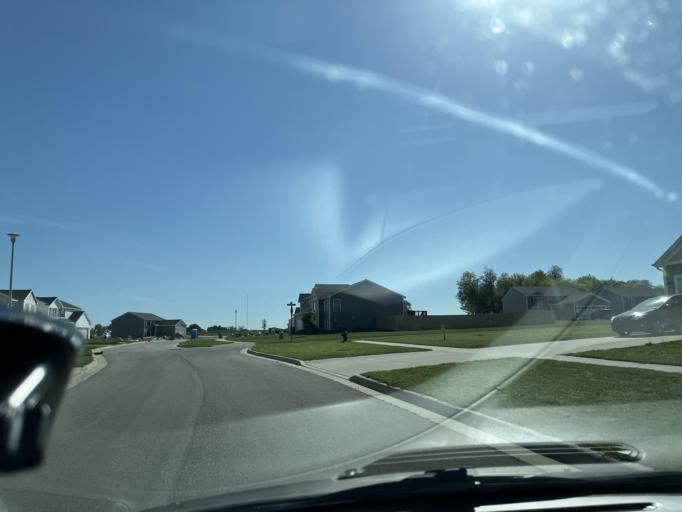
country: US
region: Michigan
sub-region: Barry County
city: Middleville
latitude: 42.7050
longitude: -85.4778
